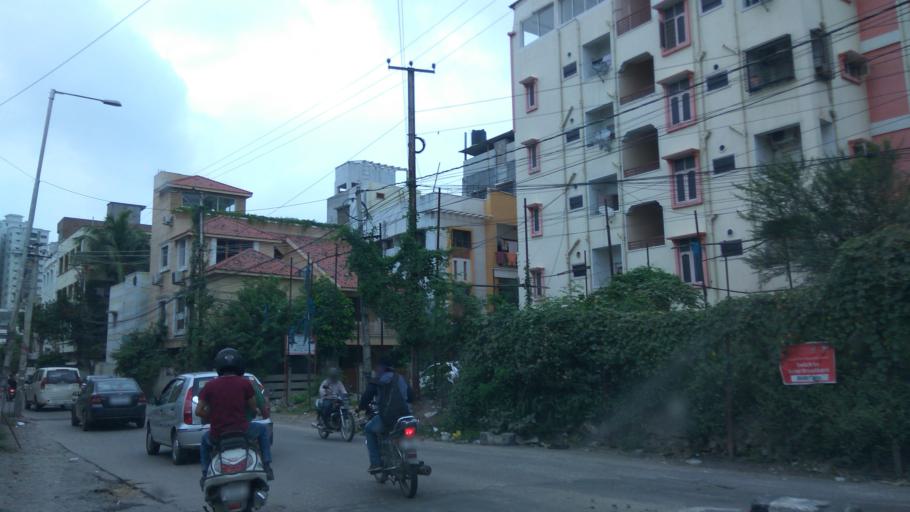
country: IN
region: Telangana
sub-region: Rangareddi
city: Kukatpalli
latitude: 17.4377
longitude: 78.3932
